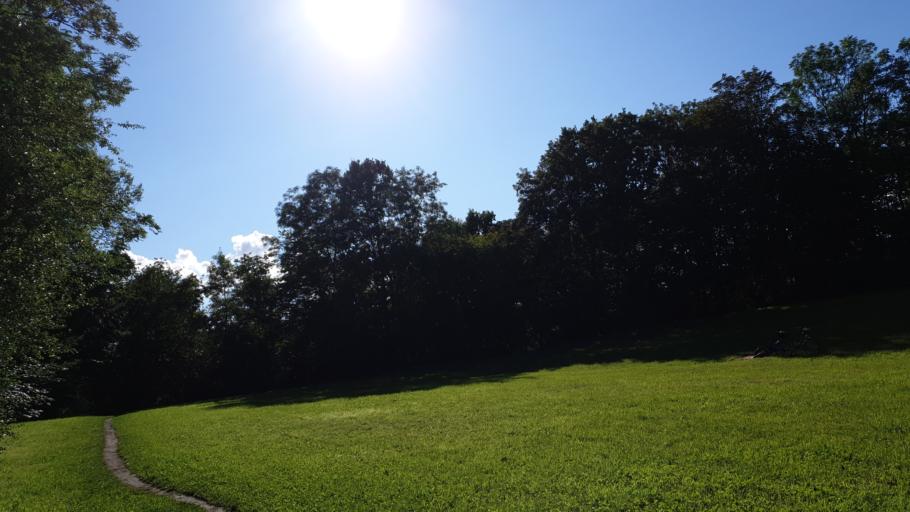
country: DE
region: Mecklenburg-Vorpommern
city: Stralsund
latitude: 54.3333
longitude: 13.0787
